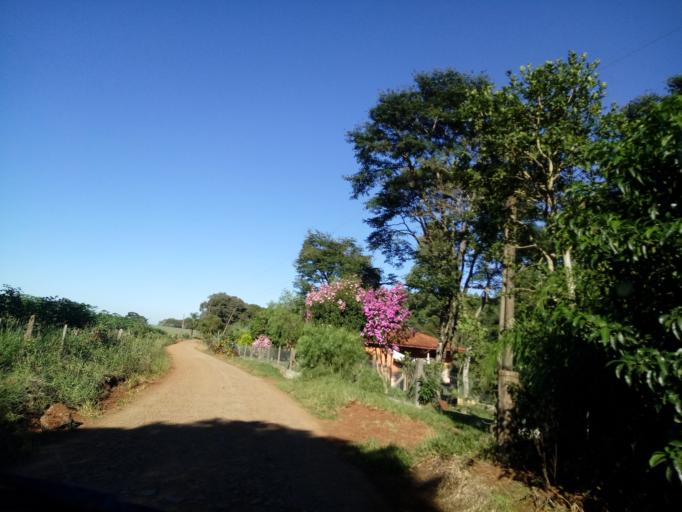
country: BR
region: Santa Catarina
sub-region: Chapeco
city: Chapeco
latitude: -27.1863
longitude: -52.7324
